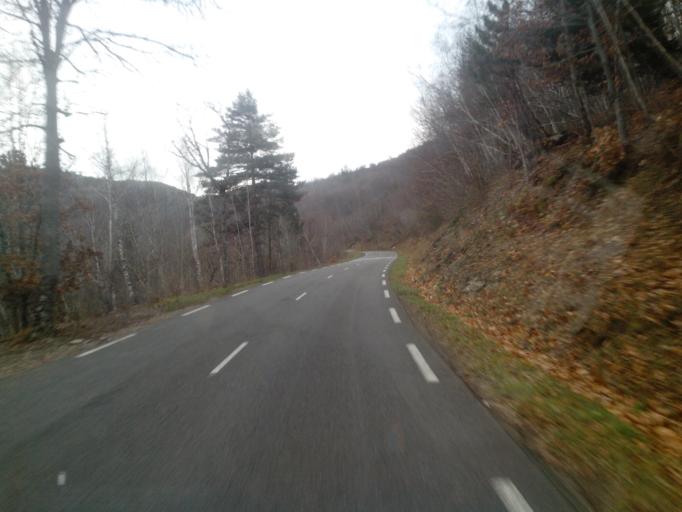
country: FR
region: Languedoc-Roussillon
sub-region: Departement de la Lozere
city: Florac
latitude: 44.2801
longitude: 3.5983
